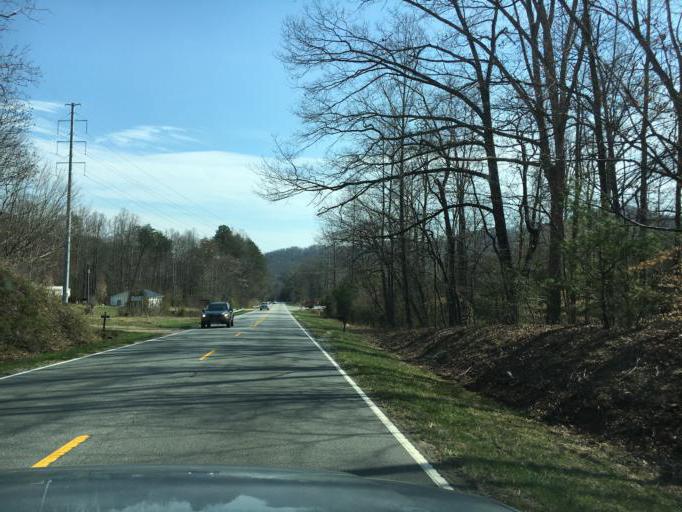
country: US
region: North Carolina
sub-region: McDowell County
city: West Marion
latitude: 35.5843
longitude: -81.9817
